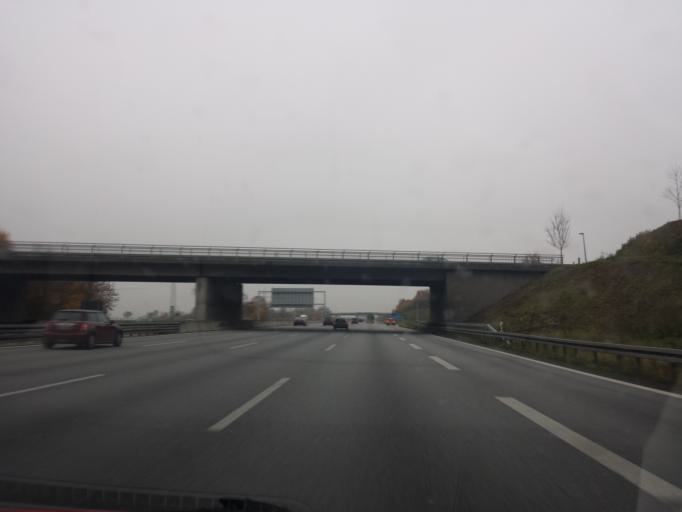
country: DE
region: Bavaria
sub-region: Upper Bavaria
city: Eching
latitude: 48.3007
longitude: 11.6302
